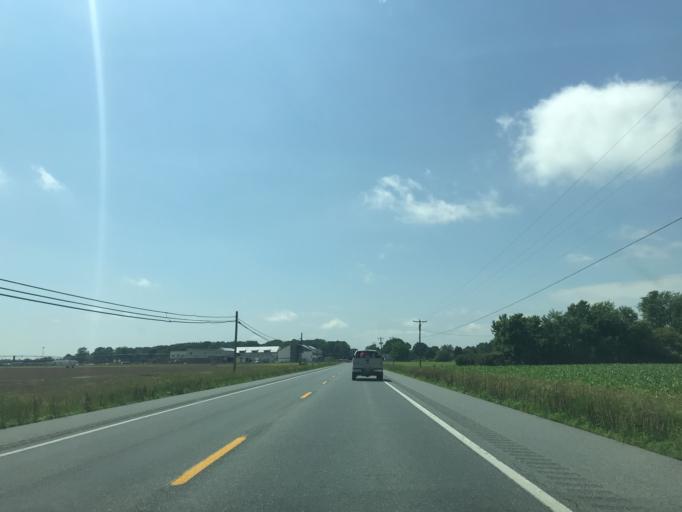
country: US
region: Maryland
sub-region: Dorchester County
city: Hurlock
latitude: 38.5871
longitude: -75.8658
